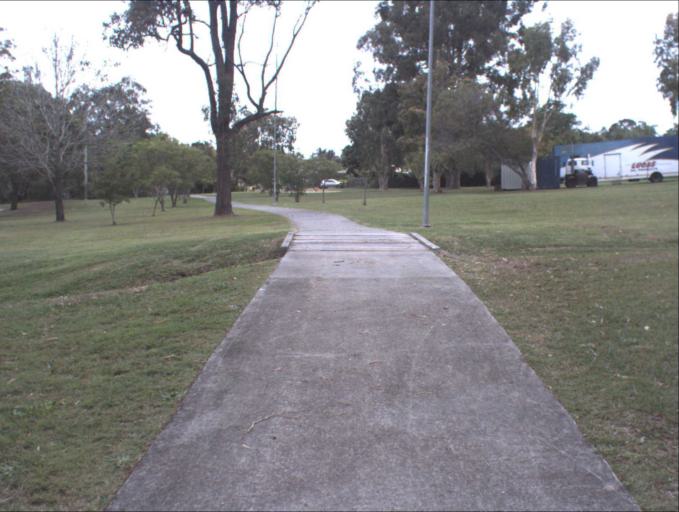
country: AU
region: Queensland
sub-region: Brisbane
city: Sunnybank Hills
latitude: -27.6606
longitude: 153.0257
